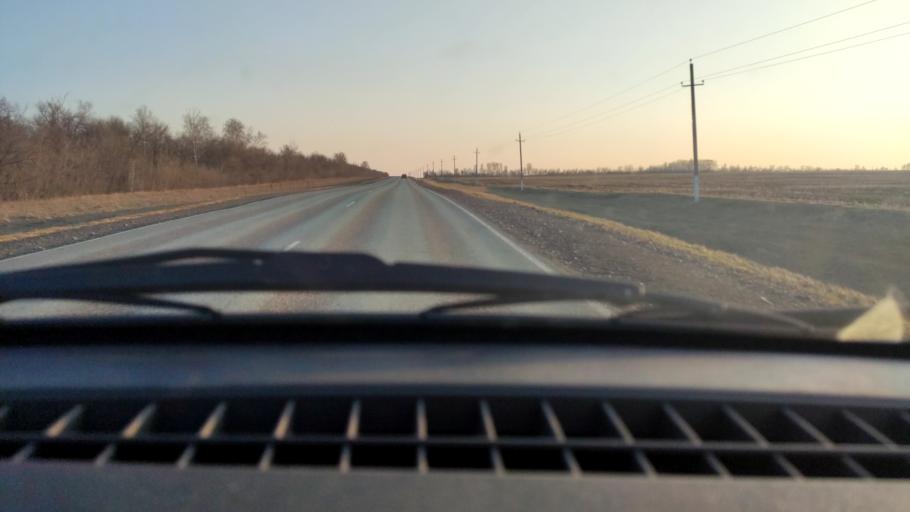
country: RU
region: Bashkortostan
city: Davlekanovo
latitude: 54.3246
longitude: 55.1600
